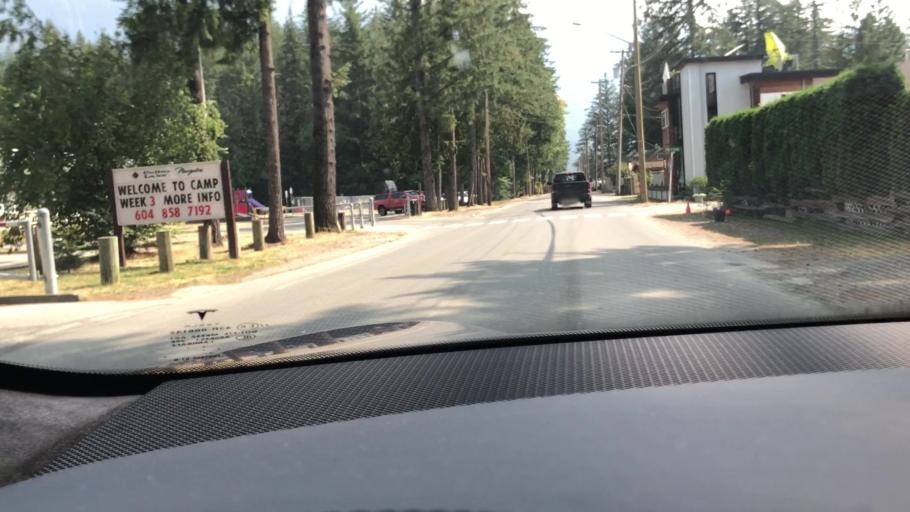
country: CA
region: British Columbia
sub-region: Fraser Valley Regional District
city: Chilliwack
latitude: 49.0729
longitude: -121.9763
